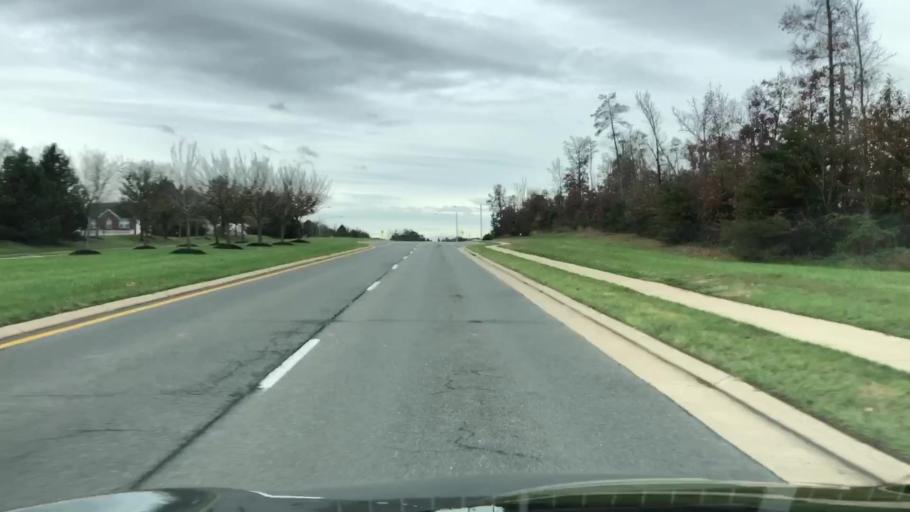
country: US
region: Virginia
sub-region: Prince William County
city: Linton Hall
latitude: 38.7390
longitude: -77.5785
